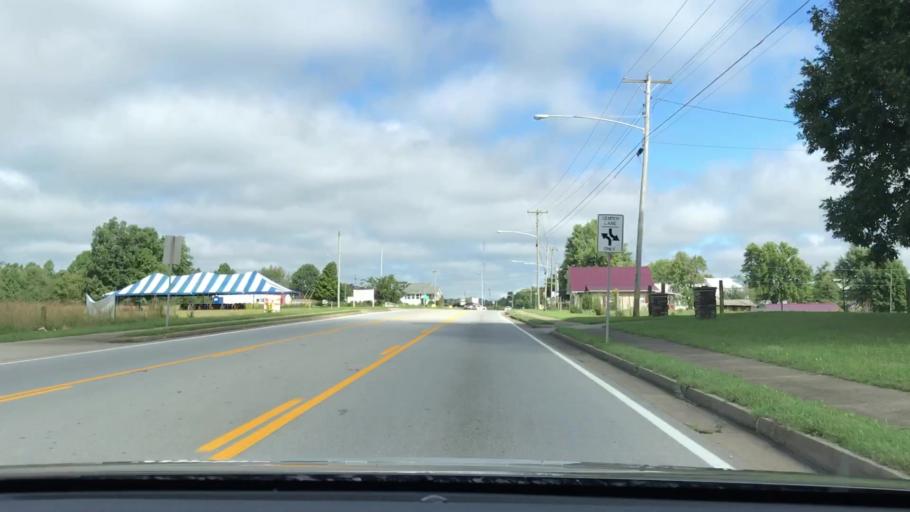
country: US
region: Kentucky
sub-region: Russell County
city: Jamestown
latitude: 37.0188
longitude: -85.0761
